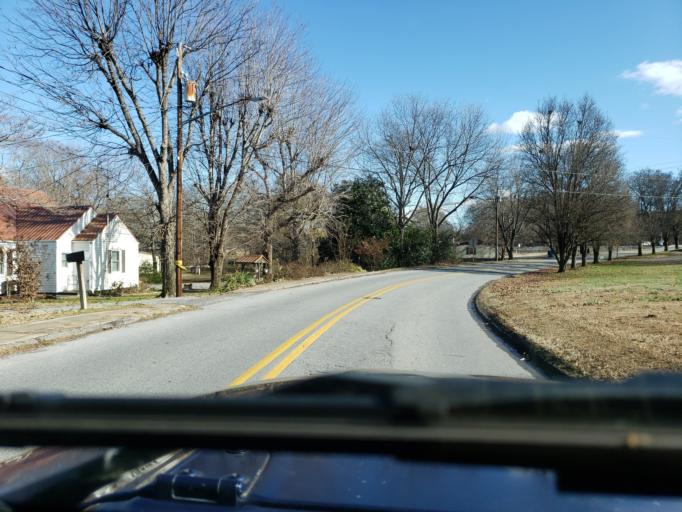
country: US
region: North Carolina
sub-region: Cleveland County
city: White Plains
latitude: 35.1730
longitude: -81.4458
